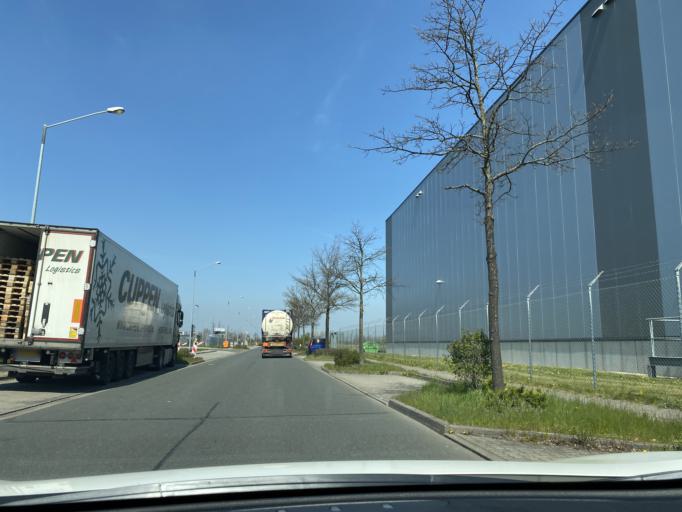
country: DE
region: Saxony
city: Zwochau
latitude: 51.3950
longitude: 12.2973
